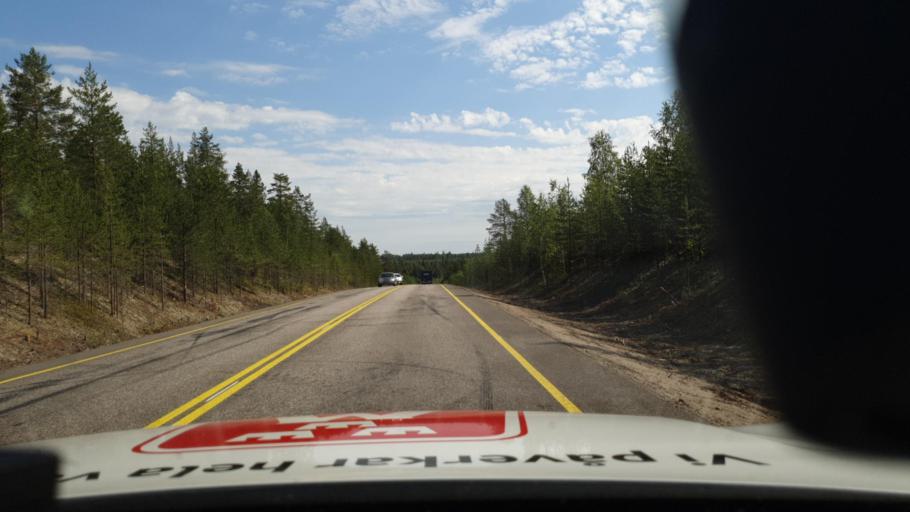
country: SE
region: Norrbotten
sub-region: Lulea Kommun
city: Ranea
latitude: 65.8684
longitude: 22.3278
